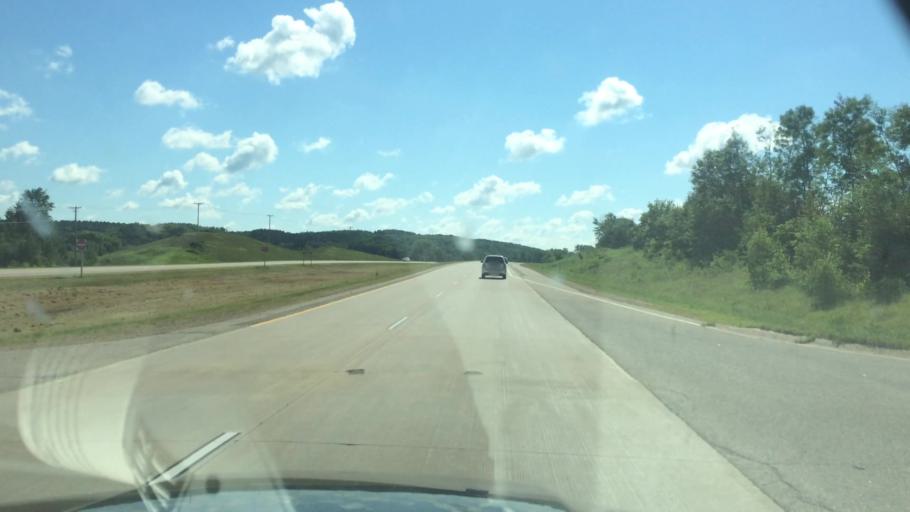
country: US
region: Wisconsin
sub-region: Portage County
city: Amherst
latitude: 44.5014
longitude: -89.3874
